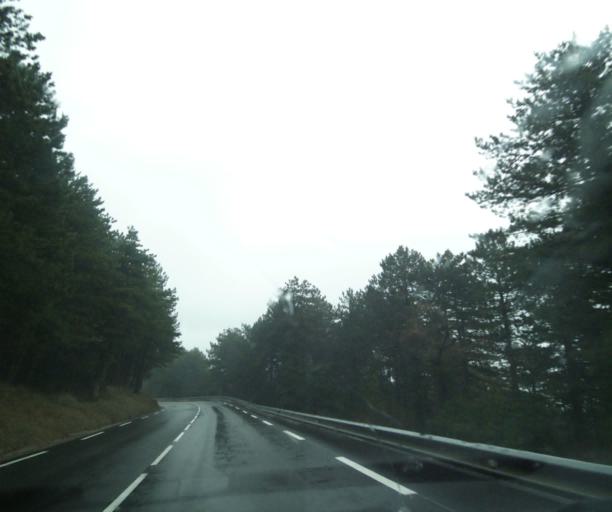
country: FR
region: Rhone-Alpes
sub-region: Departement de l'Ardeche
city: Saint-Priest
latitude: 44.7219
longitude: 4.5384
